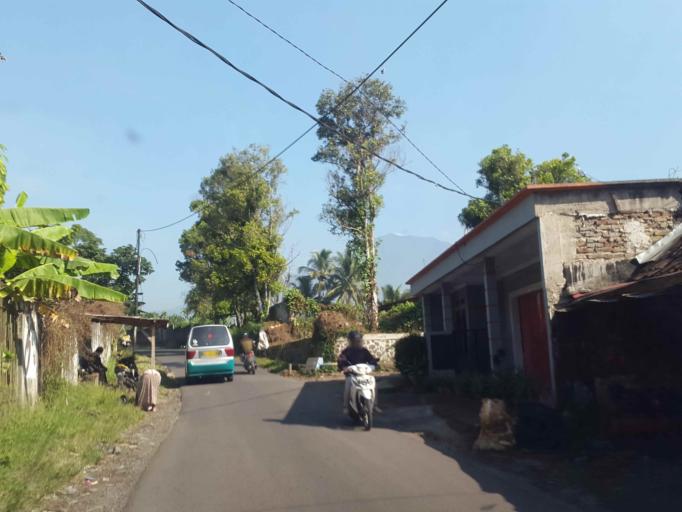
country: ID
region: West Java
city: Cibeber
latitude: -6.8660
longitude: 107.0851
